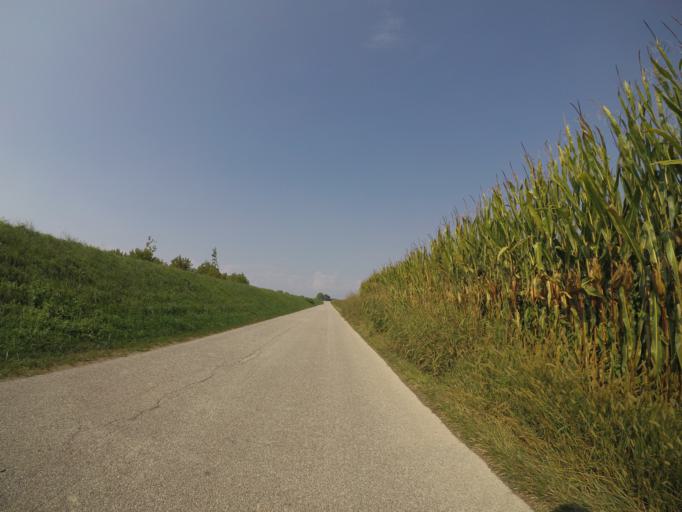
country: IT
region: Friuli Venezia Giulia
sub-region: Provincia di Udine
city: Camino al Tagliamento
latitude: 45.9385
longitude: 12.9195
